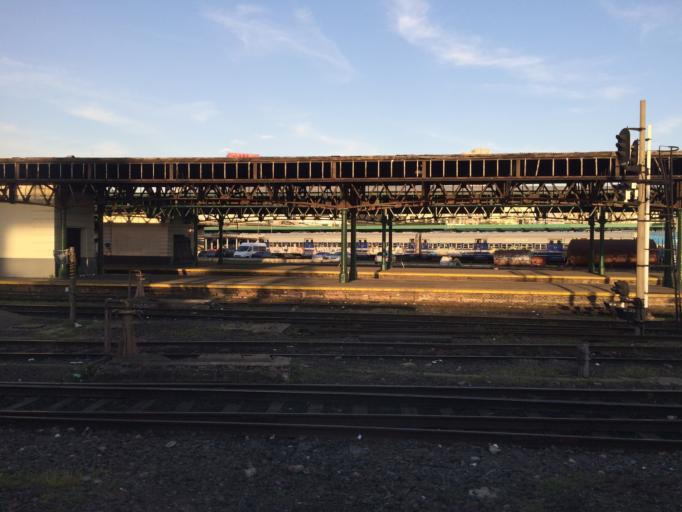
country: AR
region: Buenos Aires F.D.
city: Buenos Aires
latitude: -34.6314
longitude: -58.3804
